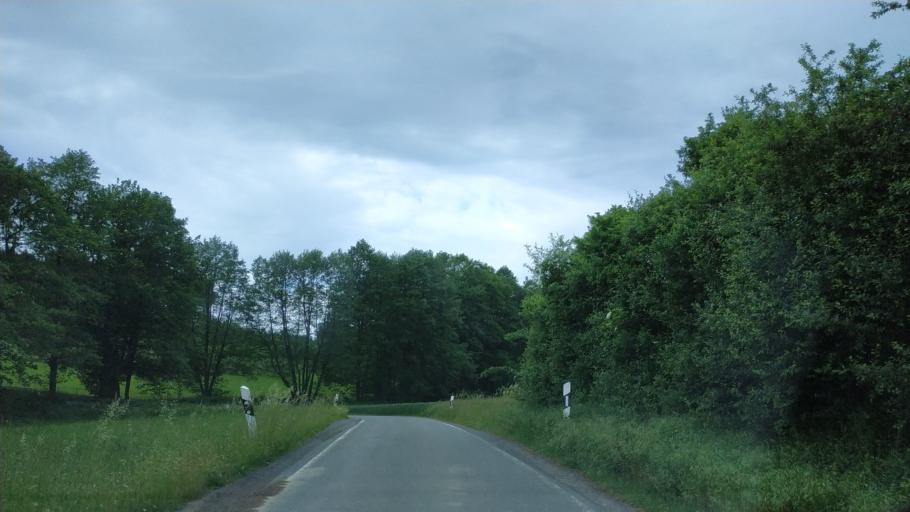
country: DE
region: Saxony
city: Syrau
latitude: 50.5404
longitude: 12.1236
